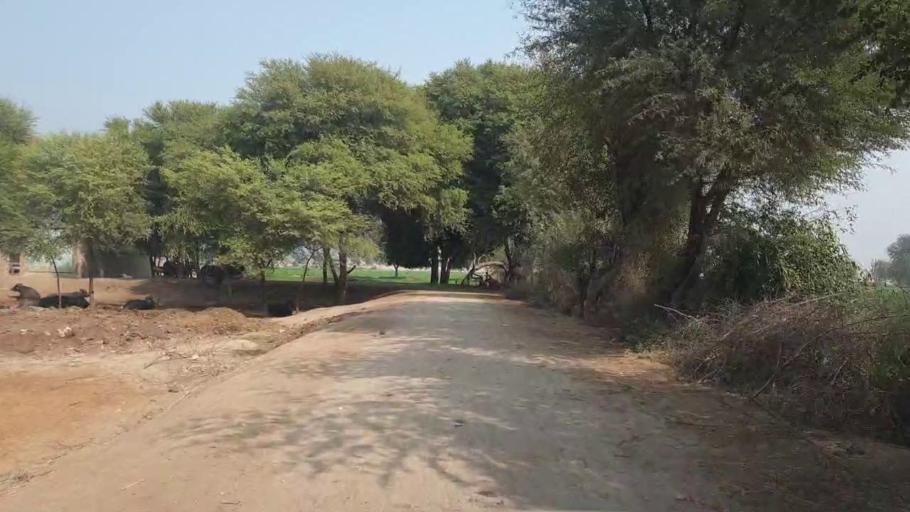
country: PK
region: Sindh
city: Hala
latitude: 25.8230
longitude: 68.4046
